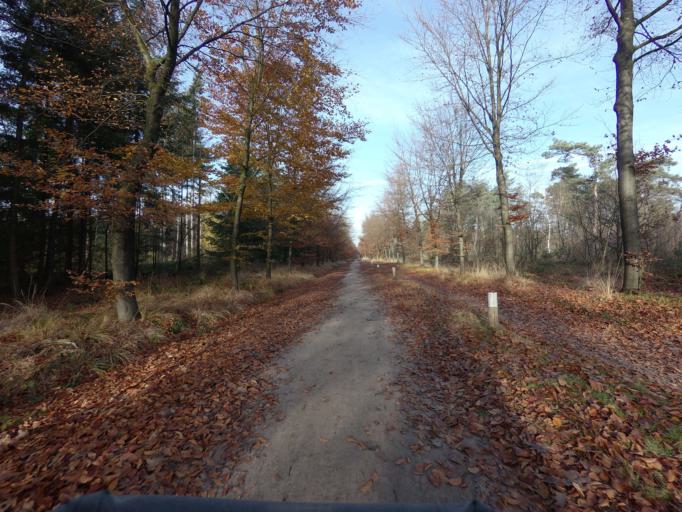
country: NL
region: North Brabant
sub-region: Gemeente Breda
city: Breda
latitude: 51.5504
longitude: 4.7701
